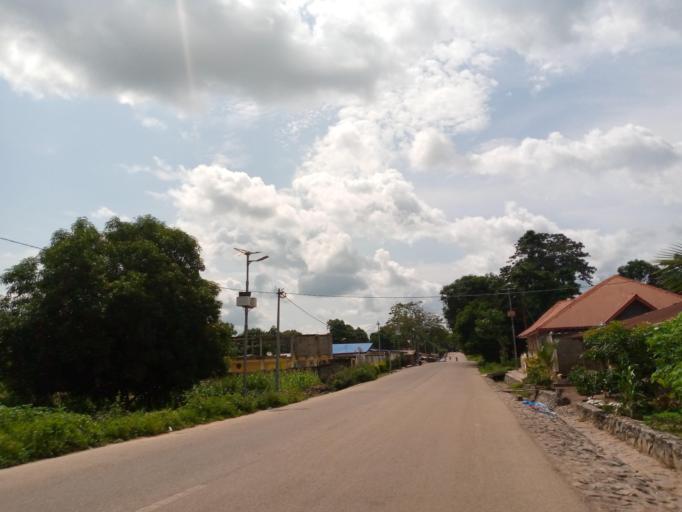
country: SL
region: Northern Province
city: Magburaka
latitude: 8.7166
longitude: -11.9374
